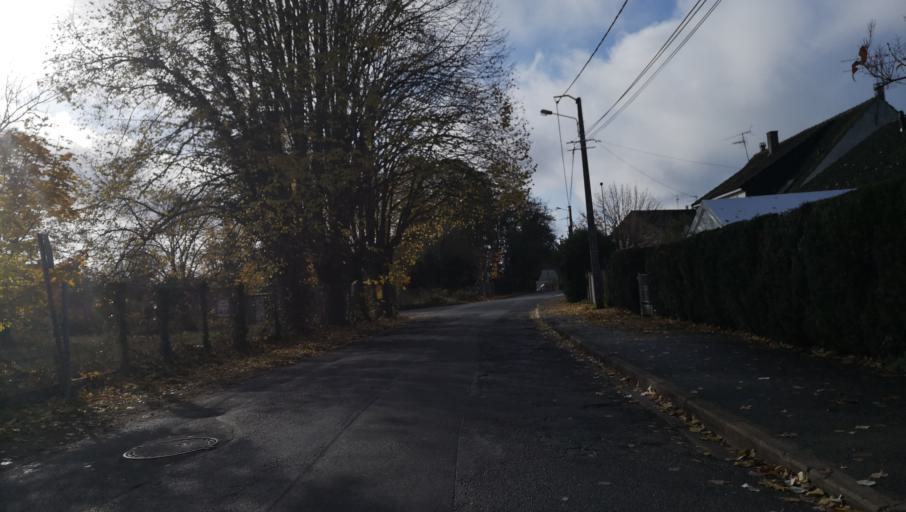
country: FR
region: Centre
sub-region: Departement du Loiret
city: Semoy
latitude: 47.9133
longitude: 1.9390
